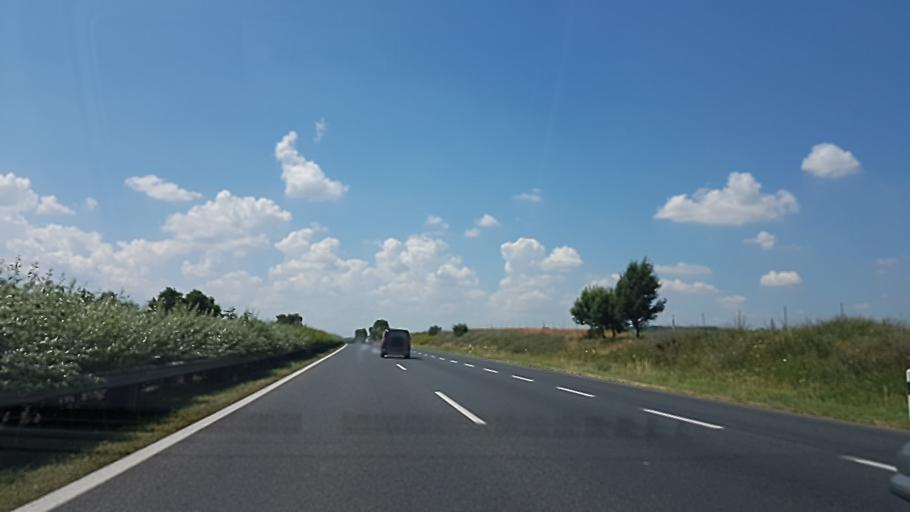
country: HU
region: Komarom-Esztergom
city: Kocs
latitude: 47.6352
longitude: 18.2411
